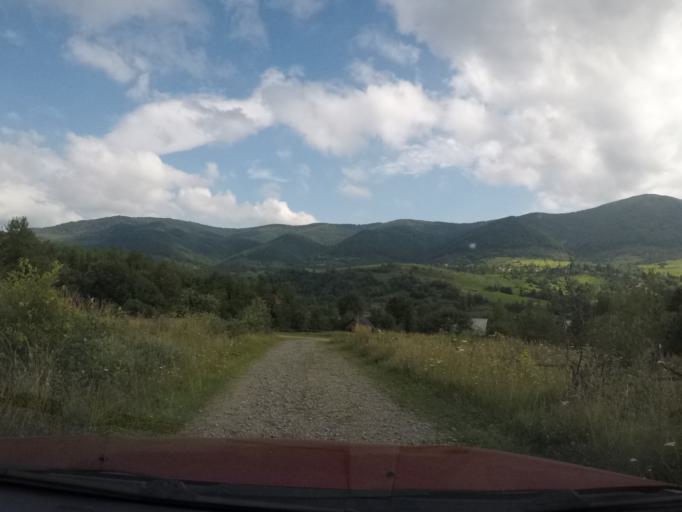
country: UA
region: Zakarpattia
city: Velykyi Bereznyi
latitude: 48.9441
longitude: 22.6753
